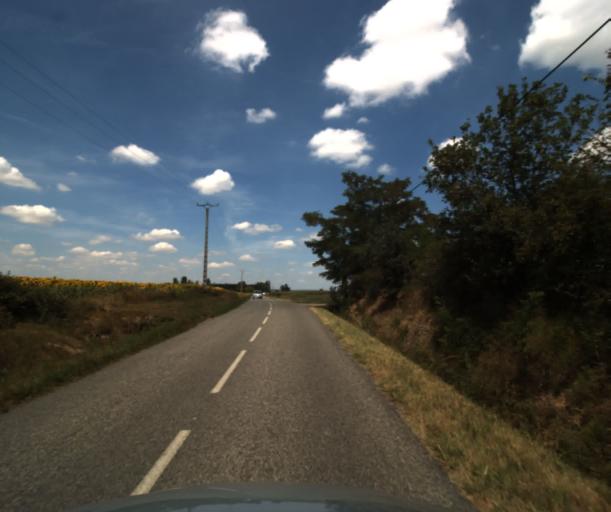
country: FR
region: Midi-Pyrenees
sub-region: Departement de la Haute-Garonne
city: Saint-Lys
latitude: 43.4875
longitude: 1.1818
